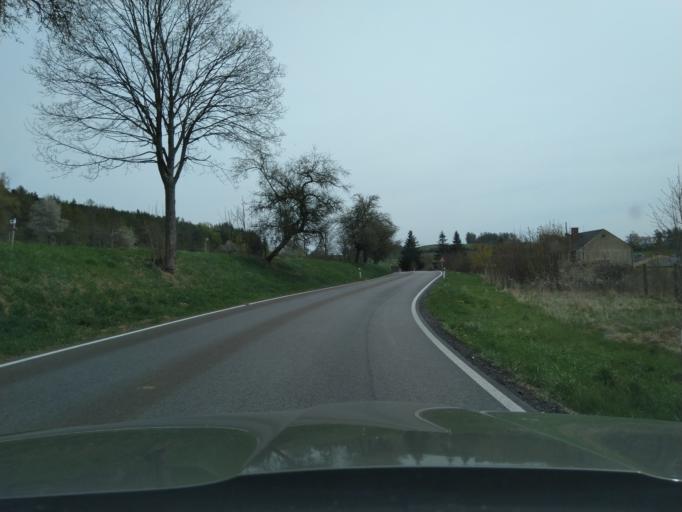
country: CZ
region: Jihocesky
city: Ckyne
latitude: 49.1175
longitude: 13.8043
